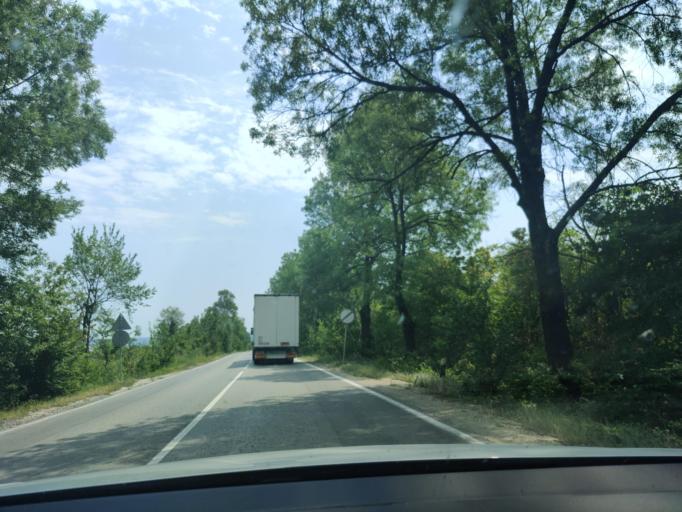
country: BG
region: Vidin
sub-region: Obshtina Ruzhintsi
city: Ruzhintsi
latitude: 43.6391
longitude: 22.7980
